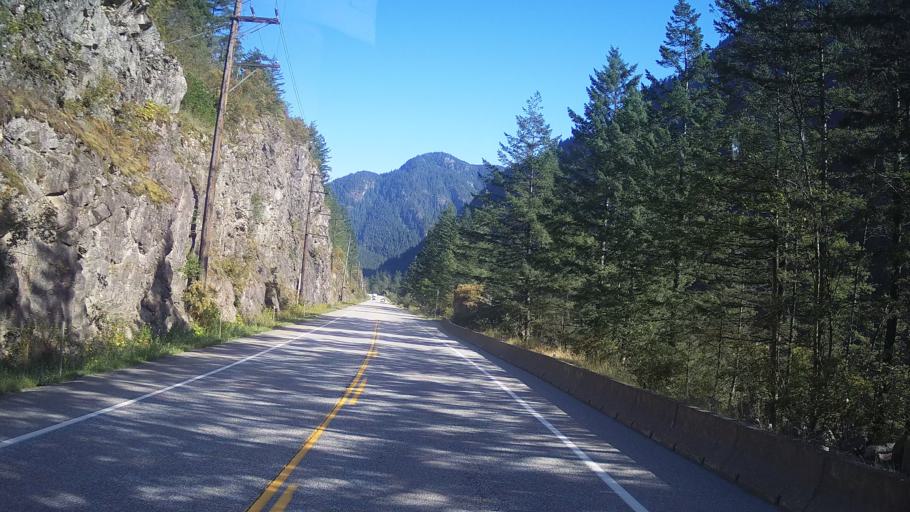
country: CA
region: British Columbia
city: Hope
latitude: 49.5807
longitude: -121.4025
